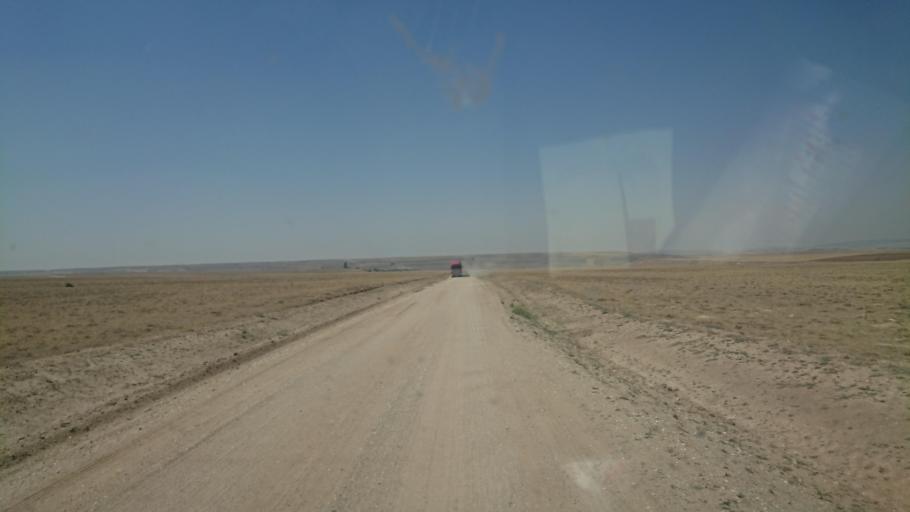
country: TR
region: Aksaray
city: Agacoren
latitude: 38.7396
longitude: 33.8808
